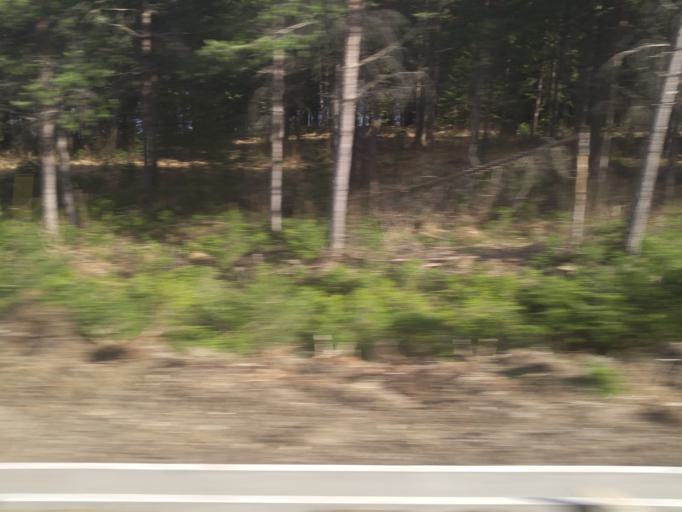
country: NO
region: Oppland
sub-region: Lillehammer
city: Lillehammer
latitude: 61.0094
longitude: 10.5476
